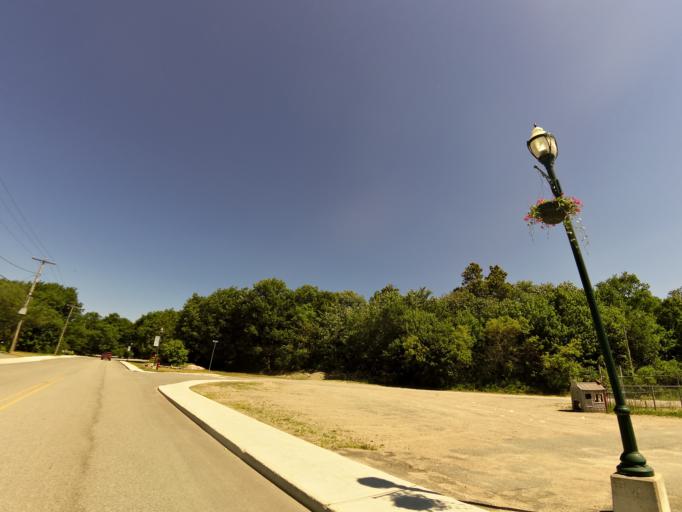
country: CA
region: Quebec
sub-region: Abitibi-Temiscamingue
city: Temiscaming
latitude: 46.7167
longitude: -79.1022
